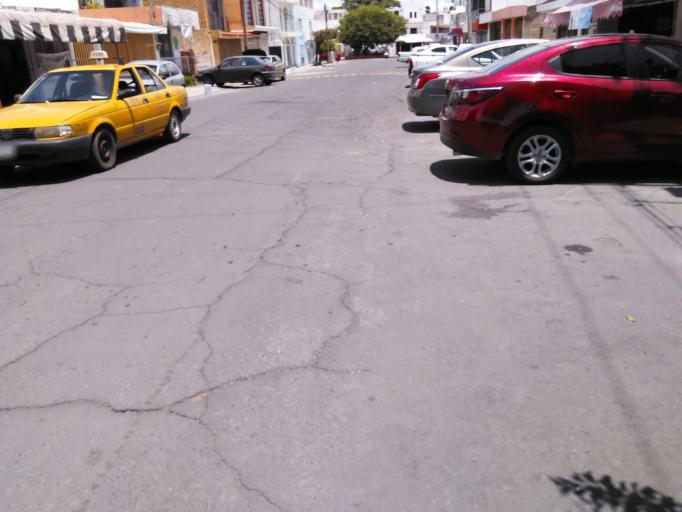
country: MX
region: Nayarit
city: Tepic
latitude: 21.5166
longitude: -104.9163
